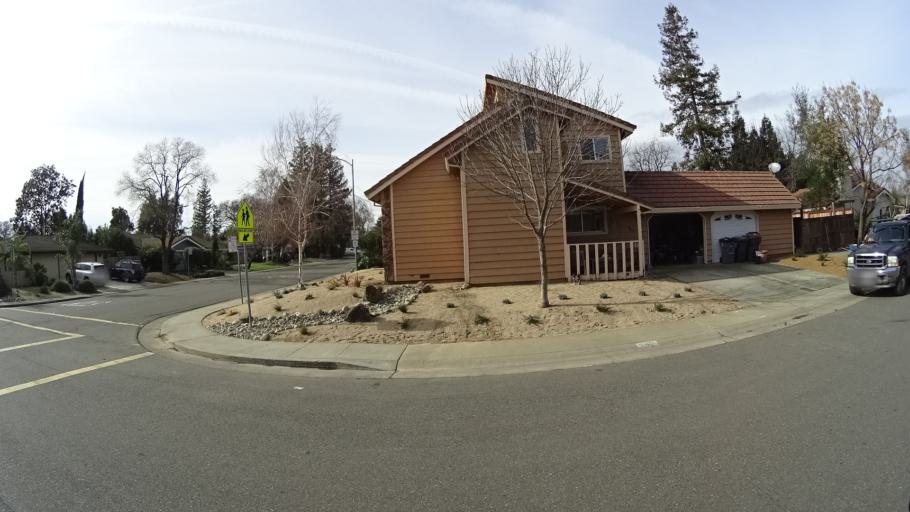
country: US
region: California
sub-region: Yolo County
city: Davis
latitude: 38.5506
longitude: -121.6836
